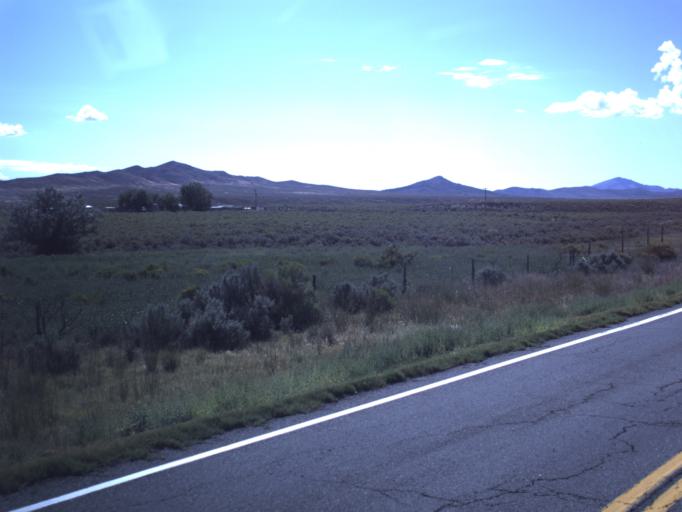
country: US
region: Utah
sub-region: Tooele County
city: Tooele
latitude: 40.1638
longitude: -112.4308
